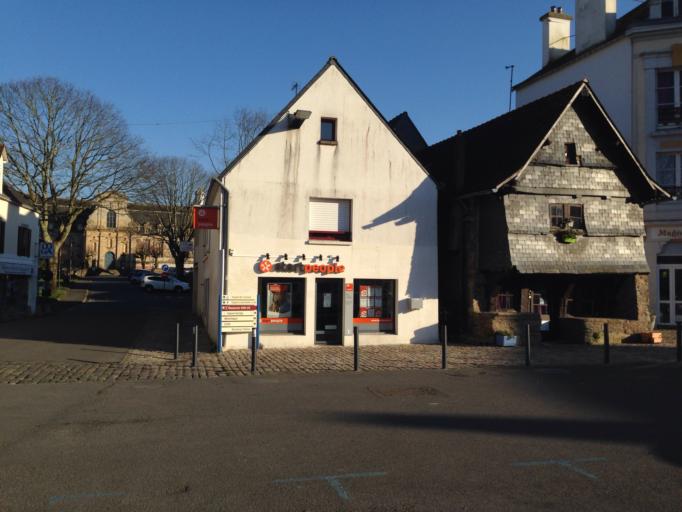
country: FR
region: Brittany
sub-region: Departement du Finistere
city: Quimperle
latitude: 47.8706
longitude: -3.5488
